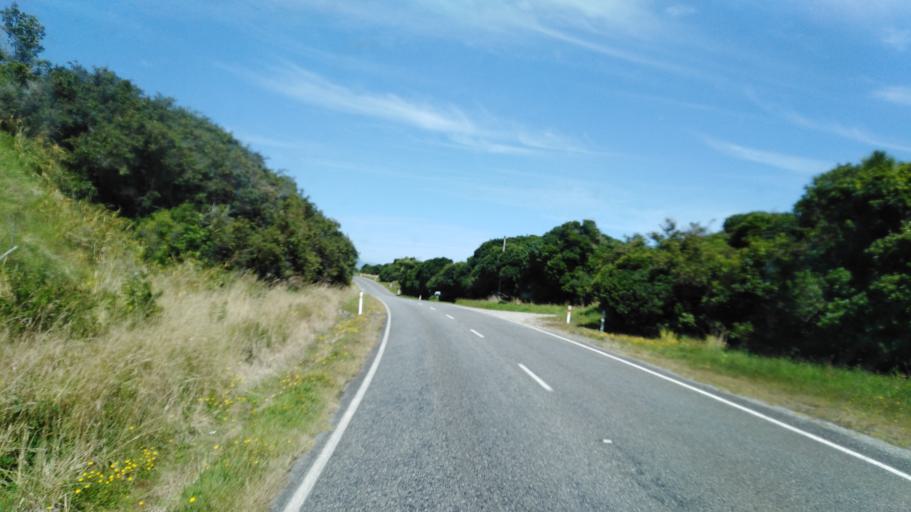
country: NZ
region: West Coast
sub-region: Buller District
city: Westport
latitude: -41.5754
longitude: 171.9018
